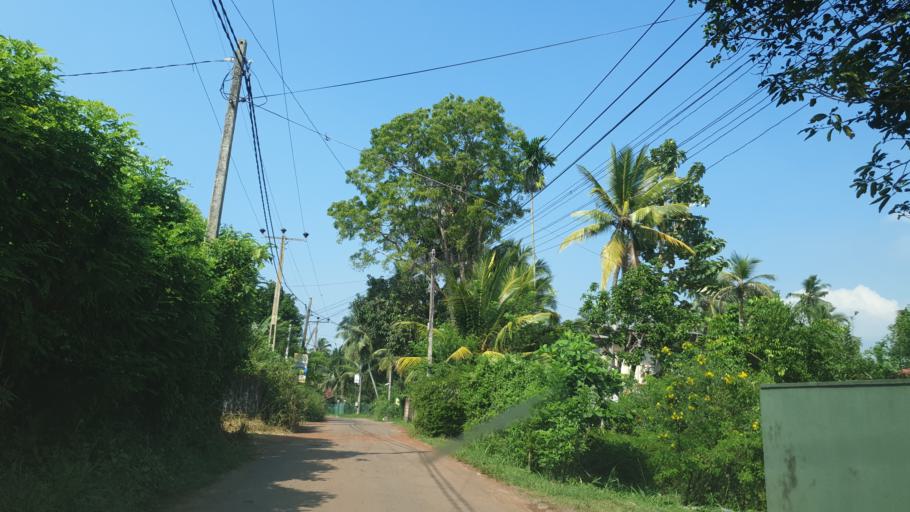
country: LK
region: Western
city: Moratuwa
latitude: 6.7618
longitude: 79.9244
